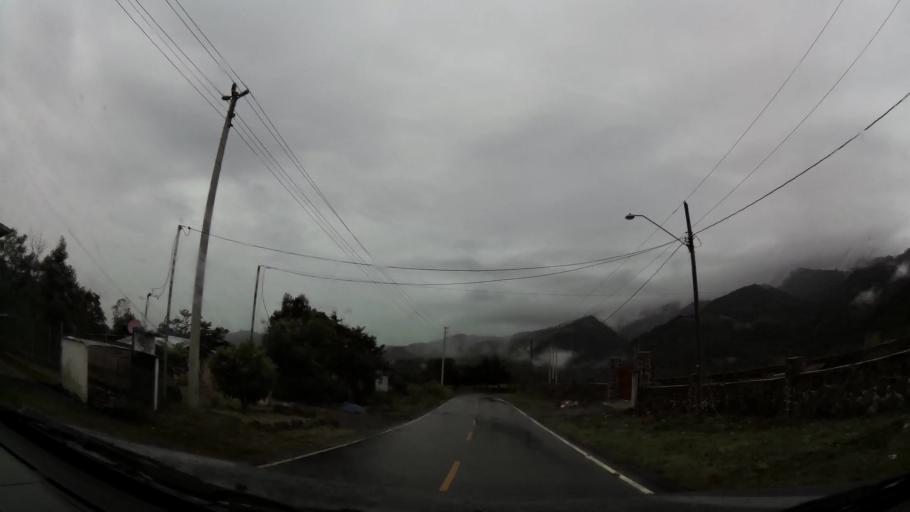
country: PA
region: Chiriqui
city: Volcan
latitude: 8.7981
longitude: -82.6485
